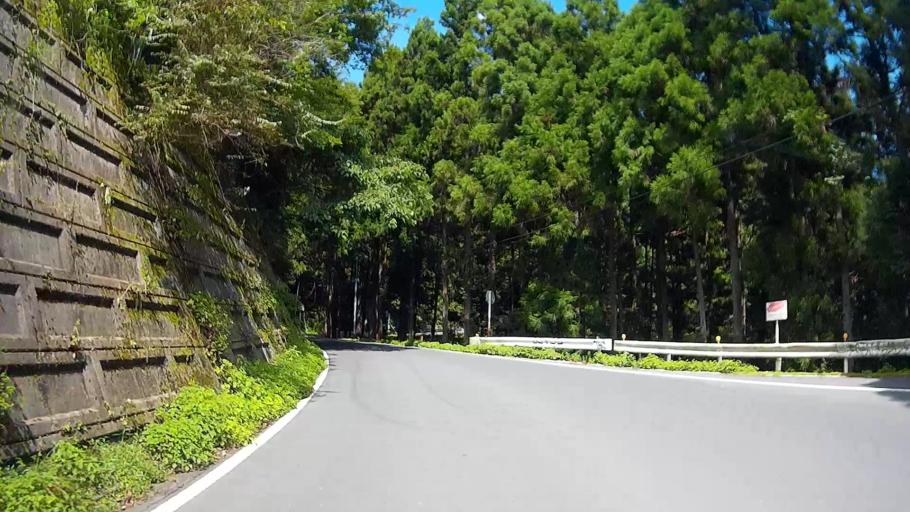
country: JP
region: Saitama
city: Chichibu
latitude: 35.9290
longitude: 139.1517
